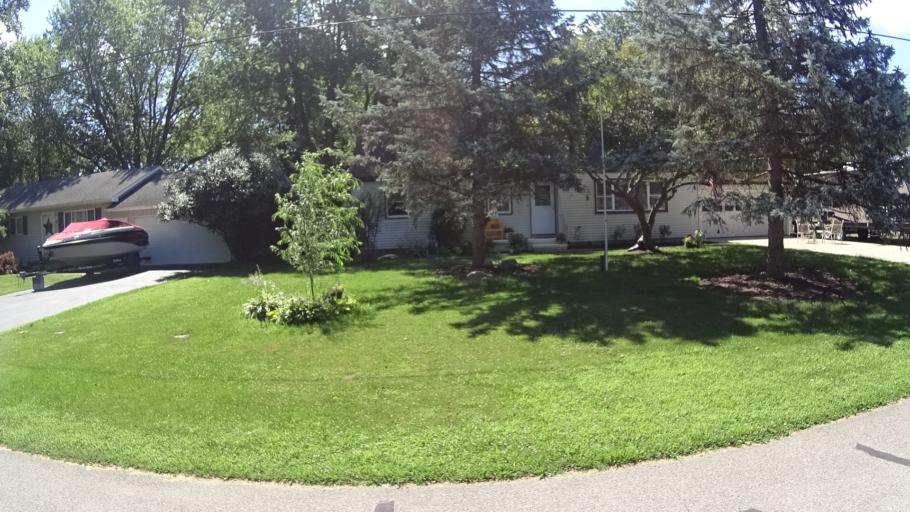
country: US
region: Ohio
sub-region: Erie County
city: Huron
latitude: 41.3789
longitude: -82.5610
